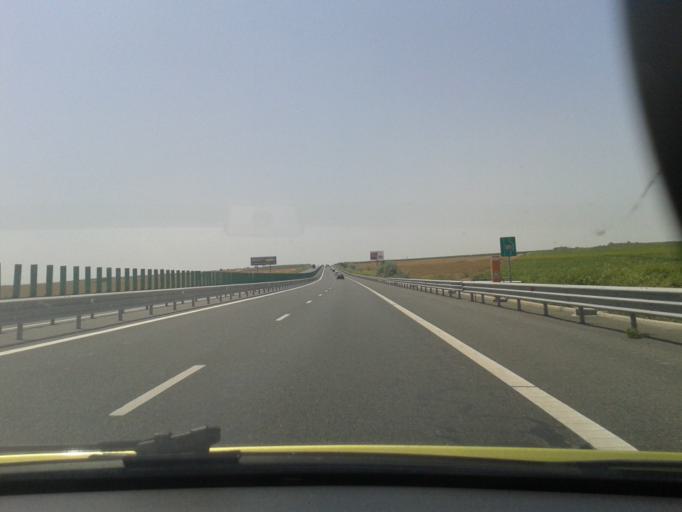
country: RO
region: Constanta
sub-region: Comuna Valu lui Traian
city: Valu lui Traian
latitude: 44.1370
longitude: 28.4337
